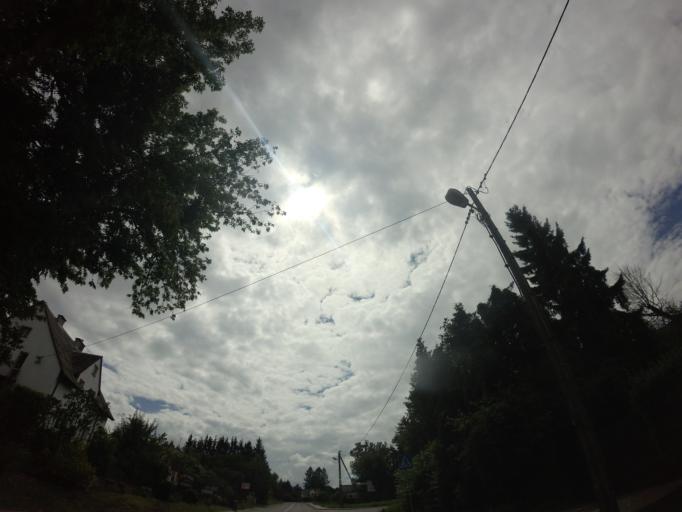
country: PL
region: Lublin Voivodeship
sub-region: Powiat pulawski
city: Kazimierz Dolny
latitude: 51.3094
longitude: 21.9496
